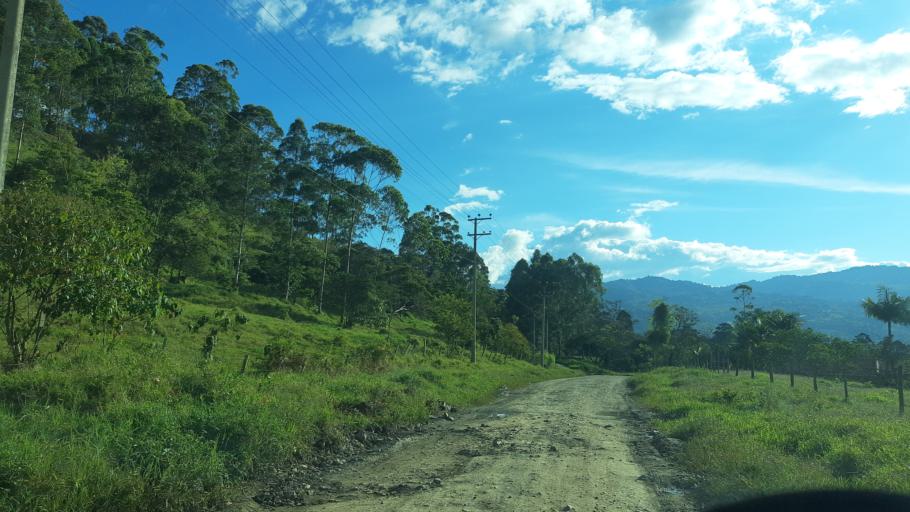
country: CO
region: Boyaca
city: Garagoa
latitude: 5.0796
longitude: -73.3719
